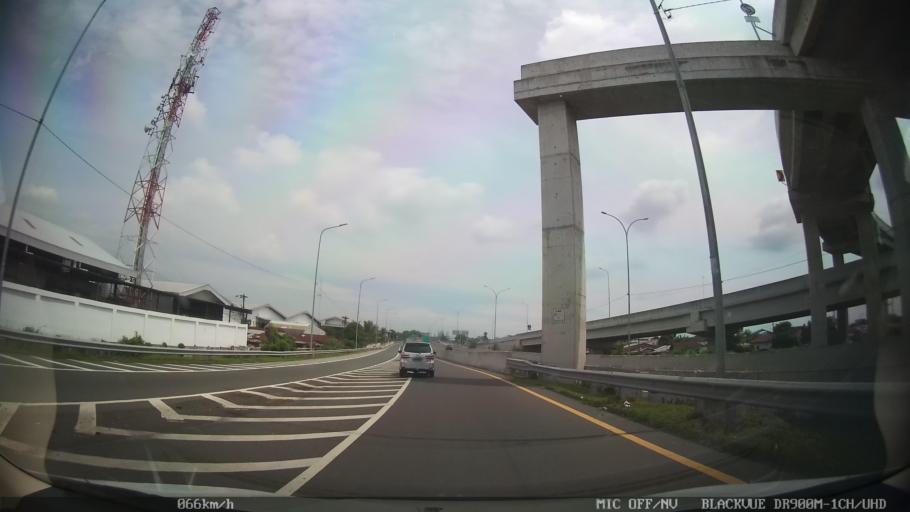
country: ID
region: North Sumatra
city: Medan
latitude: 3.6512
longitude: 98.6820
